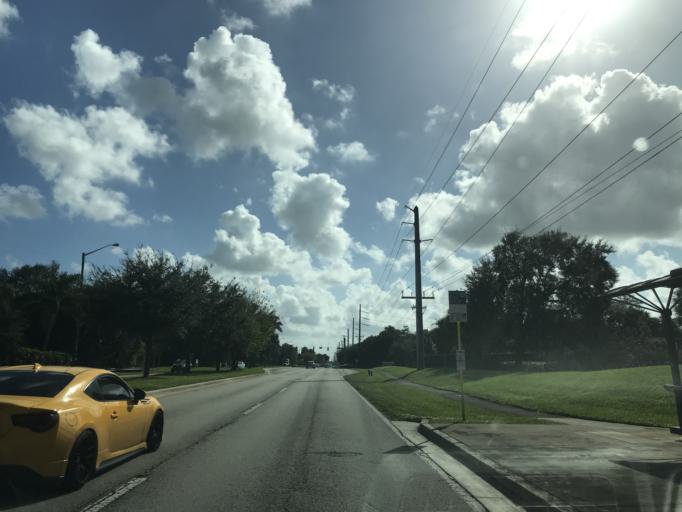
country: US
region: Florida
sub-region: Broward County
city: Coconut Creek
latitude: 26.2585
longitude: -80.1865
